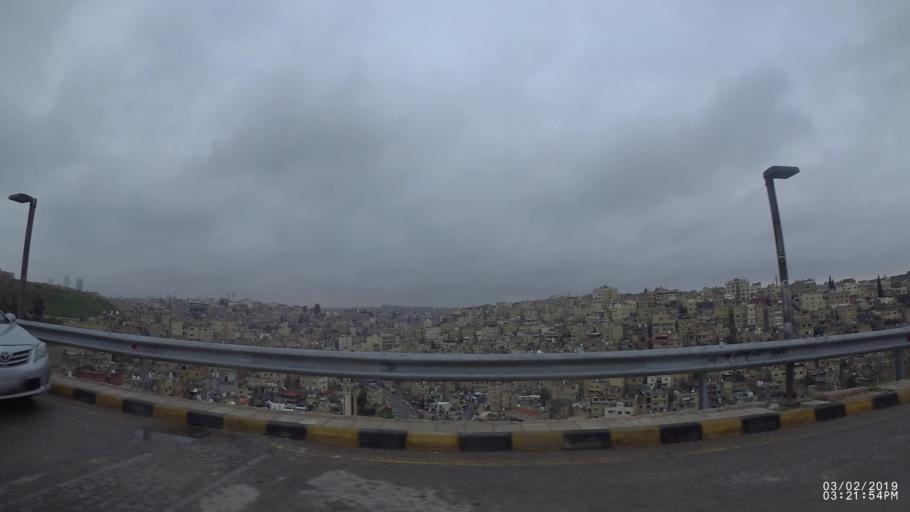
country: JO
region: Amman
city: Amman
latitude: 31.9548
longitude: 35.9379
